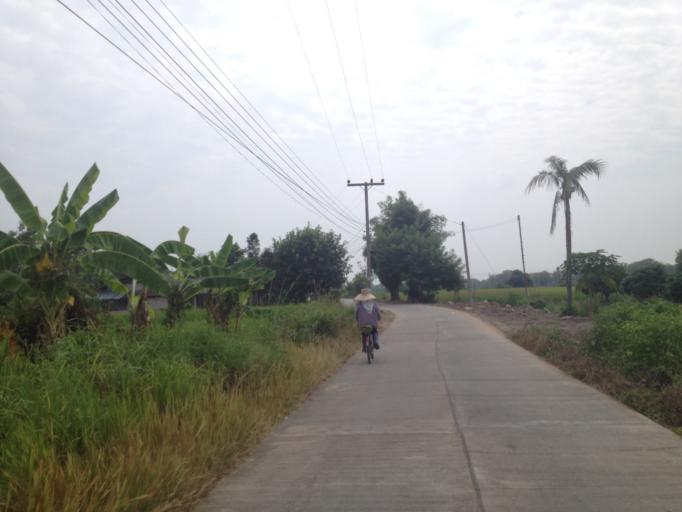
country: TH
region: Chiang Mai
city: San Pa Tong
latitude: 18.6664
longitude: 98.8851
